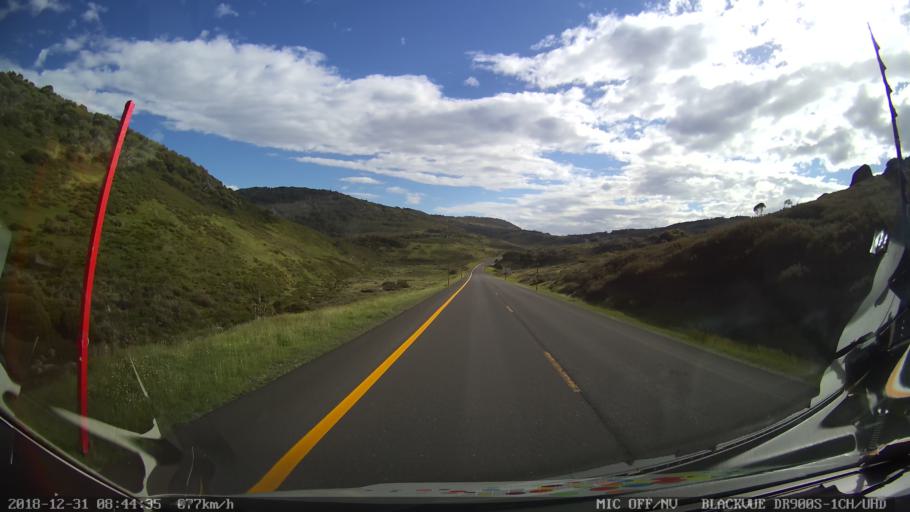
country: AU
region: New South Wales
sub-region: Snowy River
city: Jindabyne
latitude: -36.3824
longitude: 148.4561
